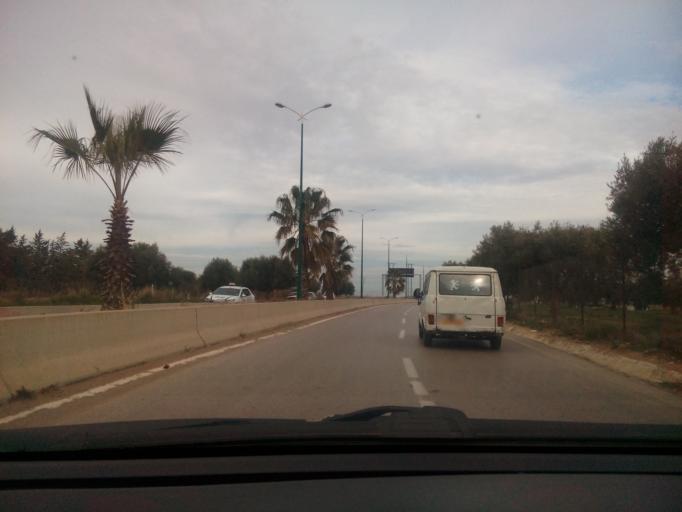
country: DZ
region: Tlemcen
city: Mansoura
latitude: 34.8676
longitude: -1.3493
